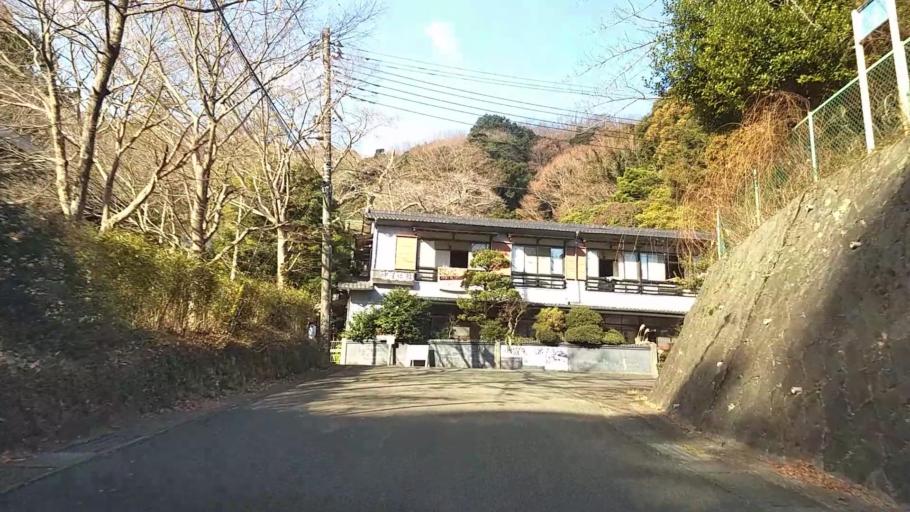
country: JP
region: Kanagawa
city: Isehara
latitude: 35.4476
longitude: 139.2878
